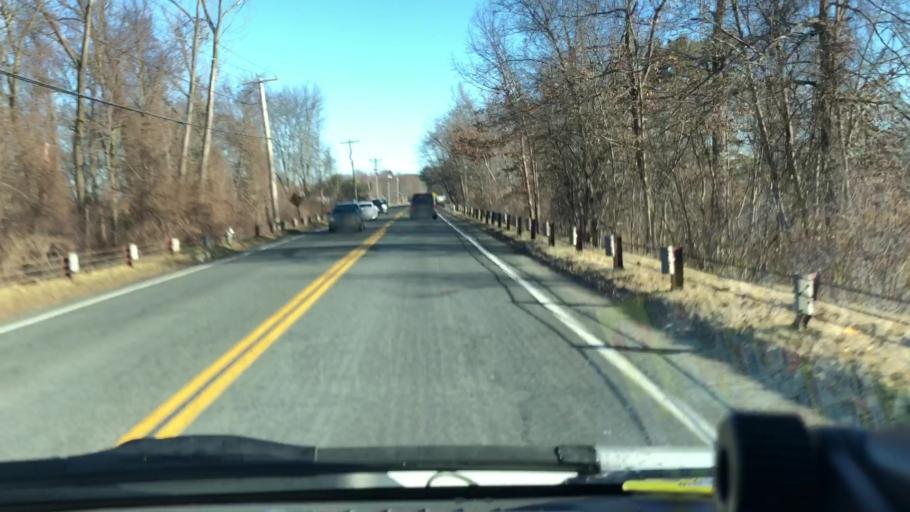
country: US
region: Massachusetts
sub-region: Hampshire County
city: North Amherst
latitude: 42.3857
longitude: -72.5480
